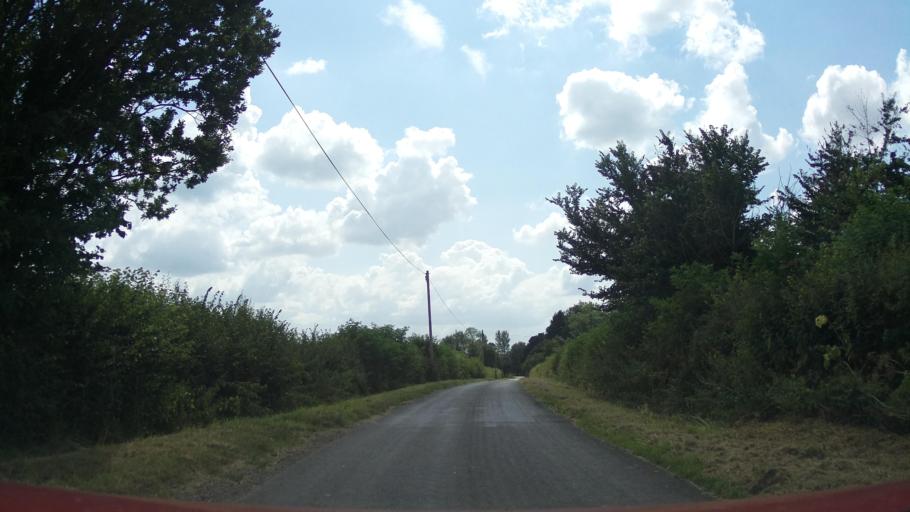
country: GB
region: England
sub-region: Wiltshire
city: Hankerton
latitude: 51.6298
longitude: -2.0305
